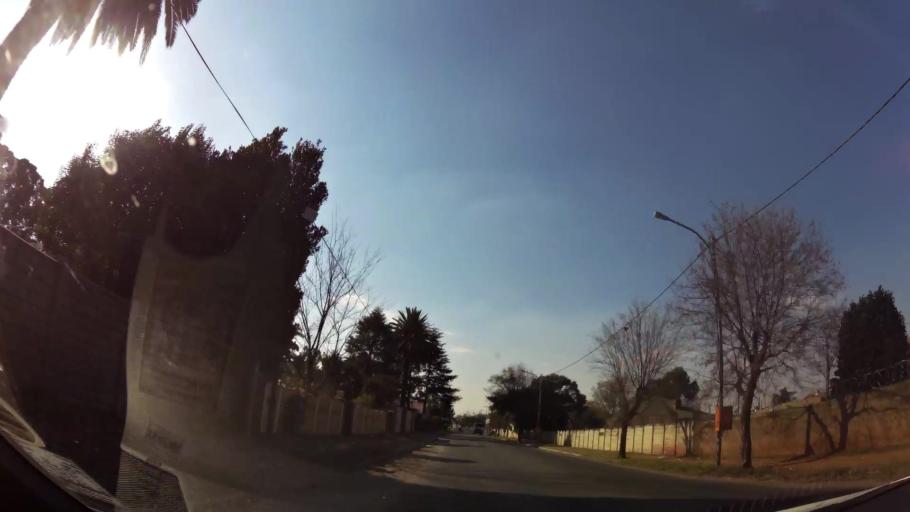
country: ZA
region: Gauteng
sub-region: Ekurhuleni Metropolitan Municipality
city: Brakpan
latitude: -26.2286
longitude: 28.3585
